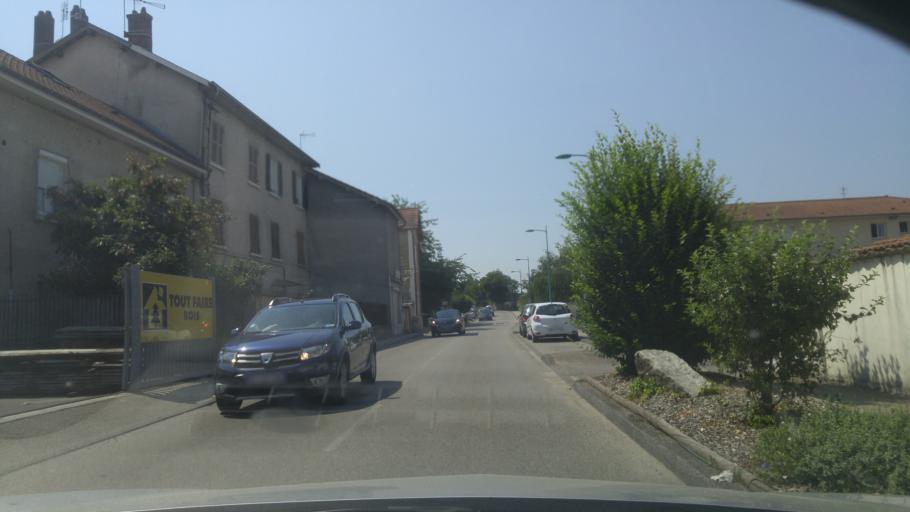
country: FR
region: Rhone-Alpes
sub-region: Departement de l'Isere
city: Pont-de-Cheruy
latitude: 45.7483
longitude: 5.1761
